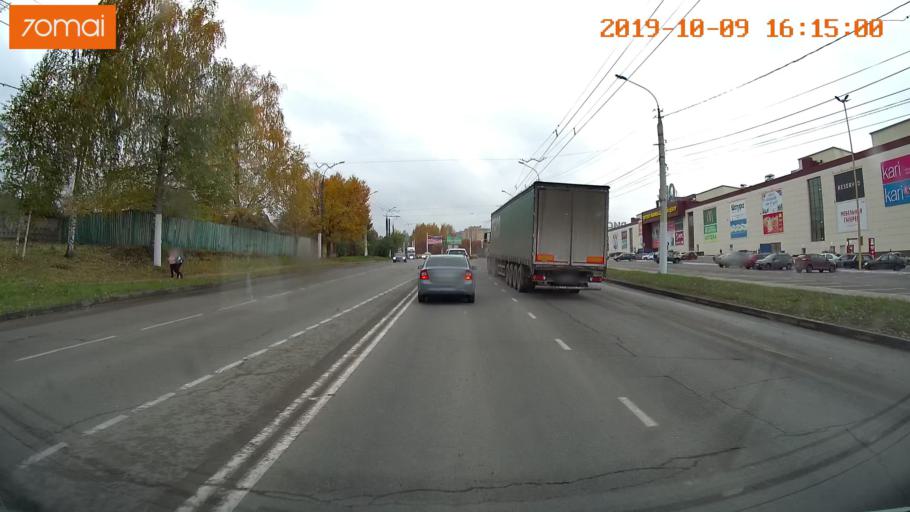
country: RU
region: Kostroma
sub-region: Kostromskoy Rayon
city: Kostroma
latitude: 57.7420
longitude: 40.9202
